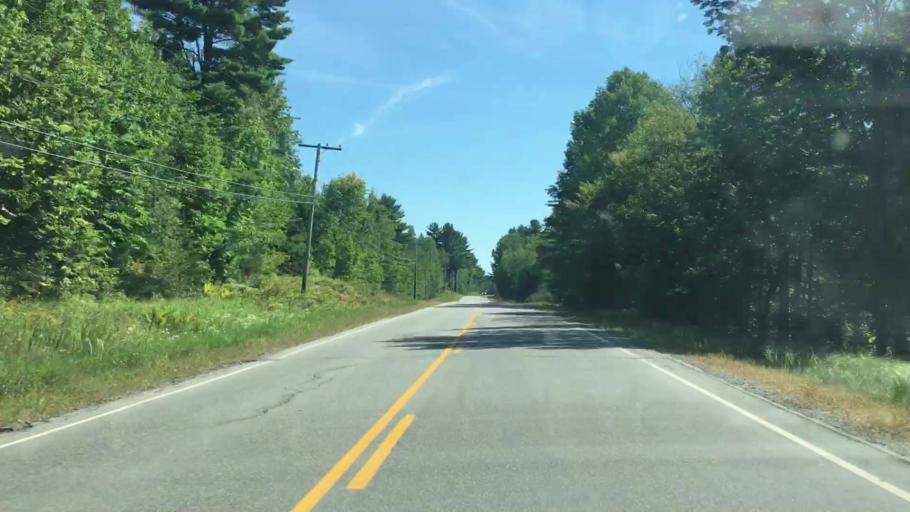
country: US
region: Maine
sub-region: Piscataquis County
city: Milo
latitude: 45.1948
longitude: -68.9020
